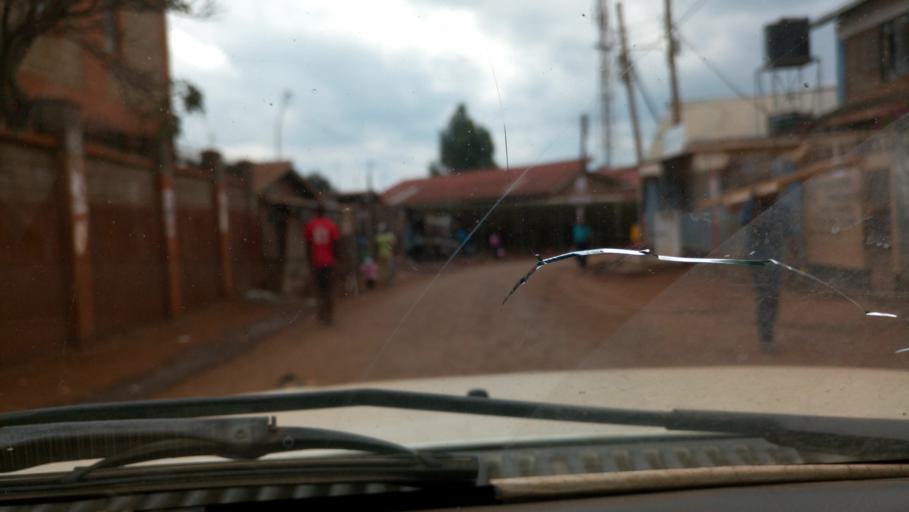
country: KE
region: Nairobi Area
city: Nairobi
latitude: -1.2726
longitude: 36.7436
